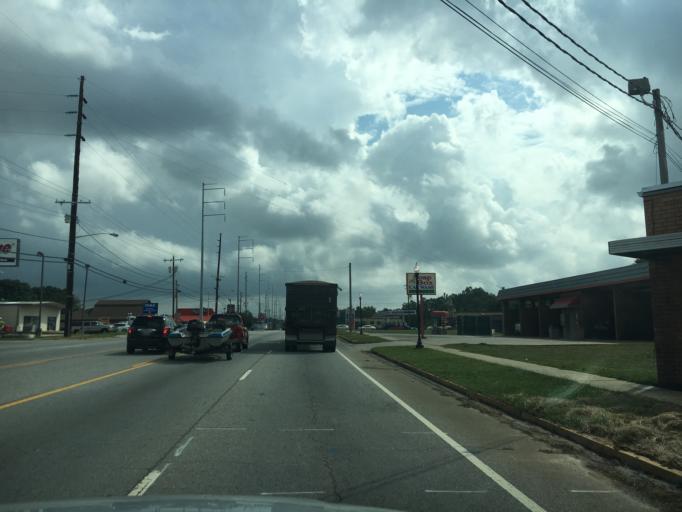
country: US
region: Georgia
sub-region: Elbert County
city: Elberton
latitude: 34.1057
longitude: -82.8546
